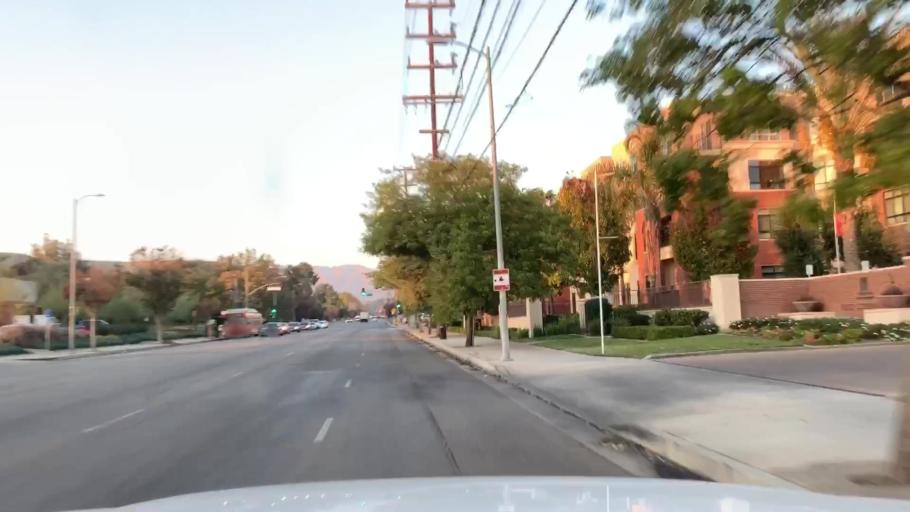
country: US
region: California
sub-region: Los Angeles County
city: Northridge
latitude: 34.2381
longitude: -118.5623
